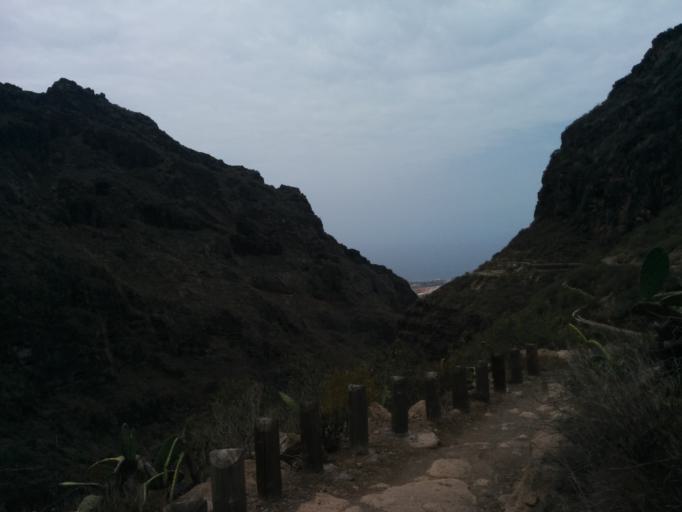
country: ES
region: Canary Islands
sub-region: Provincia de Santa Cruz de Tenerife
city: Adeje
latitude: 28.1310
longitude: -16.7149
